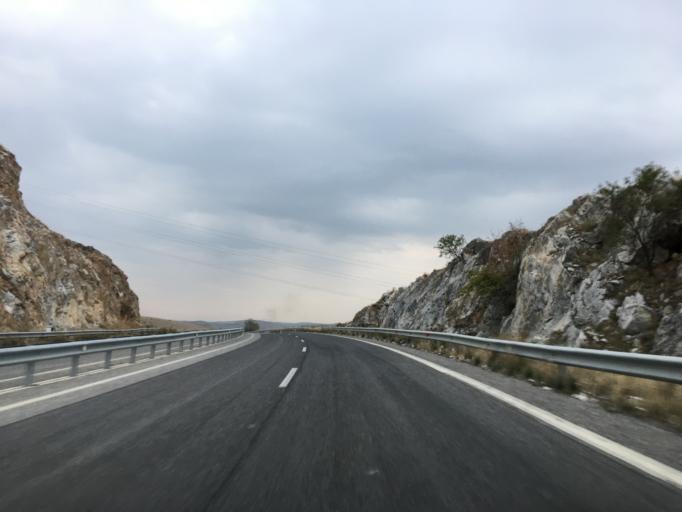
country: GR
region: Thessaly
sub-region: Trikala
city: Zarkos
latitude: 39.6097
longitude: 22.2325
